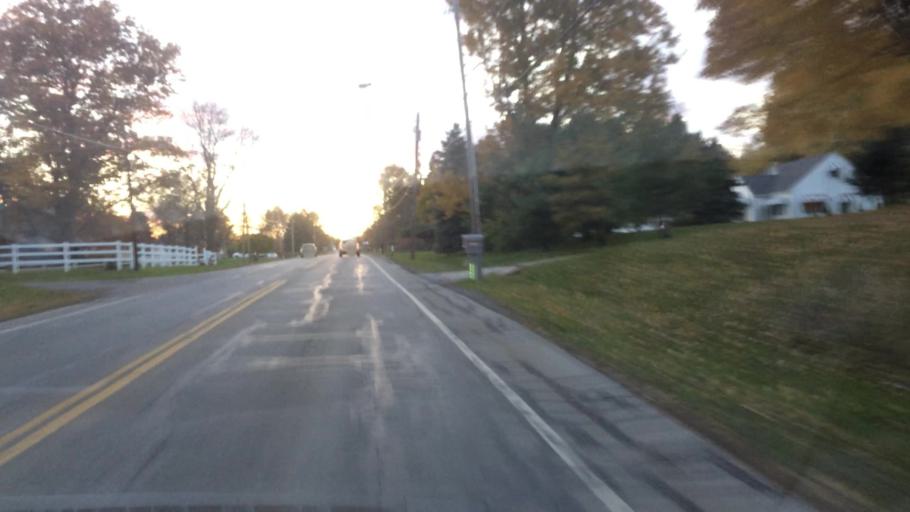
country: US
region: Ohio
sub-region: Summit County
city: Norton
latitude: 41.0498
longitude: -81.6558
